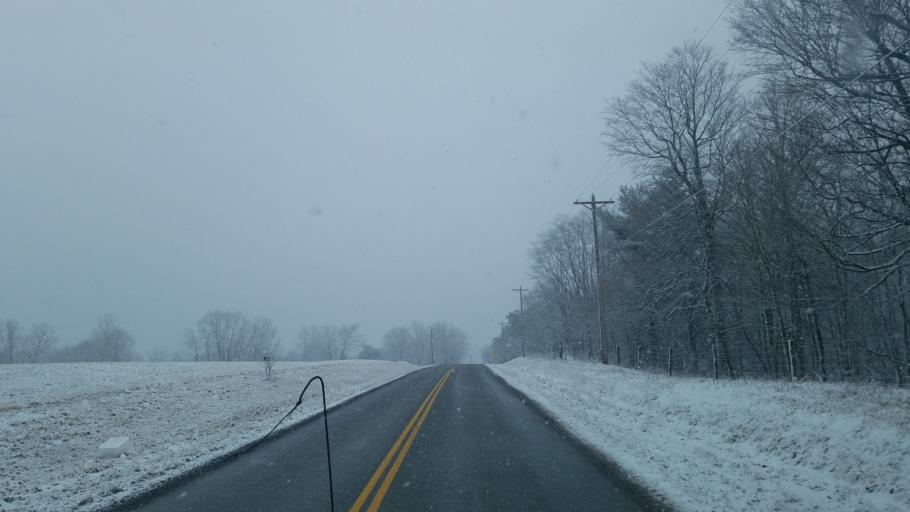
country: US
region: Ohio
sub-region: Logan County
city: Bellefontaine
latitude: 40.3375
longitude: -83.6568
